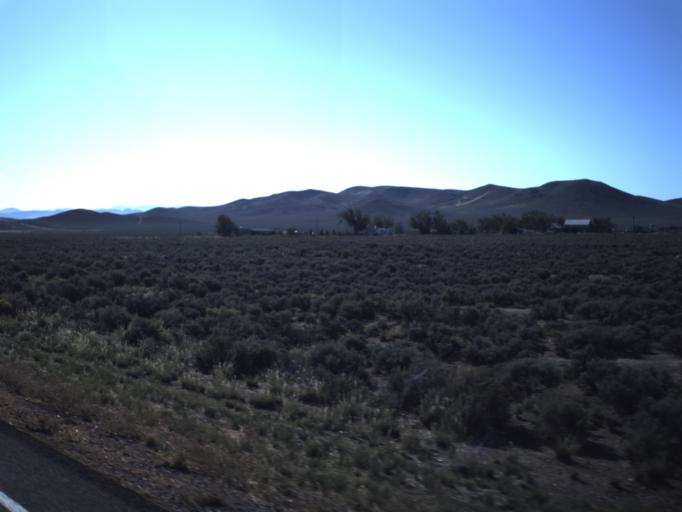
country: US
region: Utah
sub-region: Washington County
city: Enterprise
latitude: 37.7495
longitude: -113.7684
